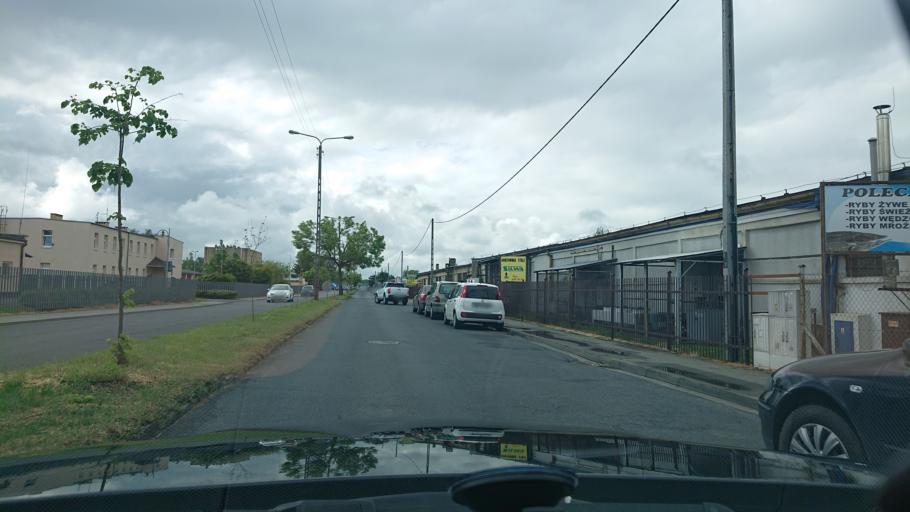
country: PL
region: Greater Poland Voivodeship
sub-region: Powiat gnieznienski
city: Gniezno
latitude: 52.5385
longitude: 17.6254
